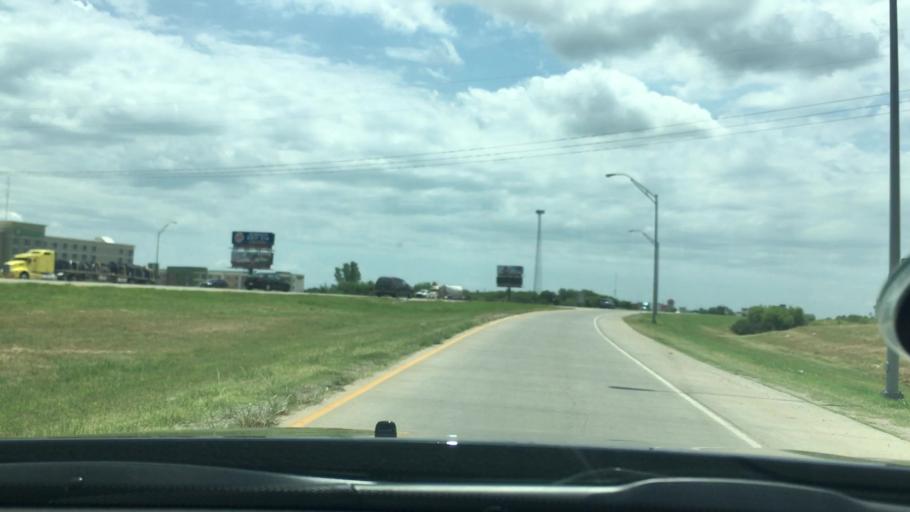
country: US
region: Oklahoma
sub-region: Carter County
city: Ardmore
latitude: 34.2000
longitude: -97.1646
